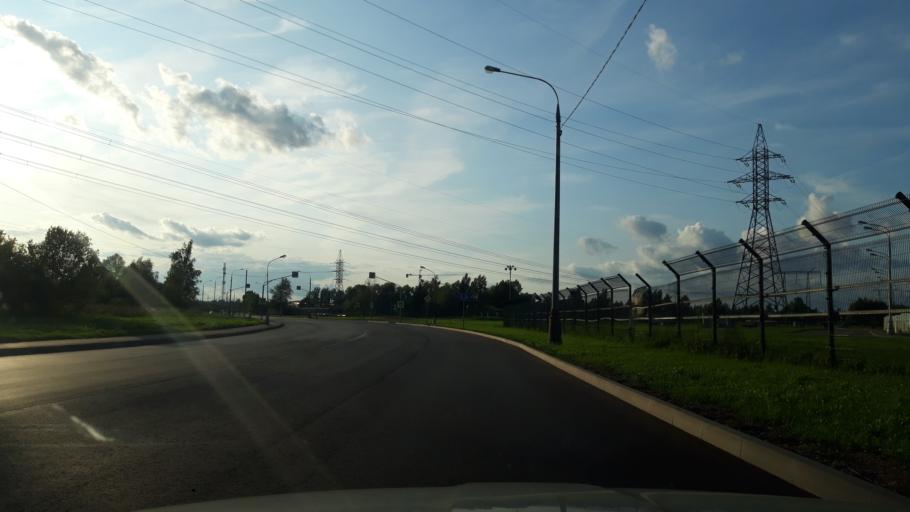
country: RU
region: Moskovskaya
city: Alabushevo
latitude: 56.0008
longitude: 37.1550
